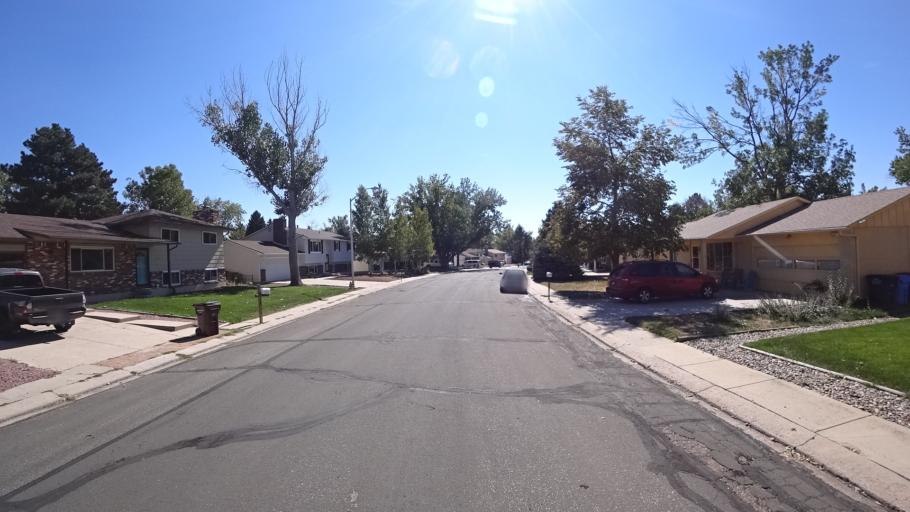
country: US
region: Colorado
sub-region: El Paso County
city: Cimarron Hills
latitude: 38.9038
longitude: -104.7640
